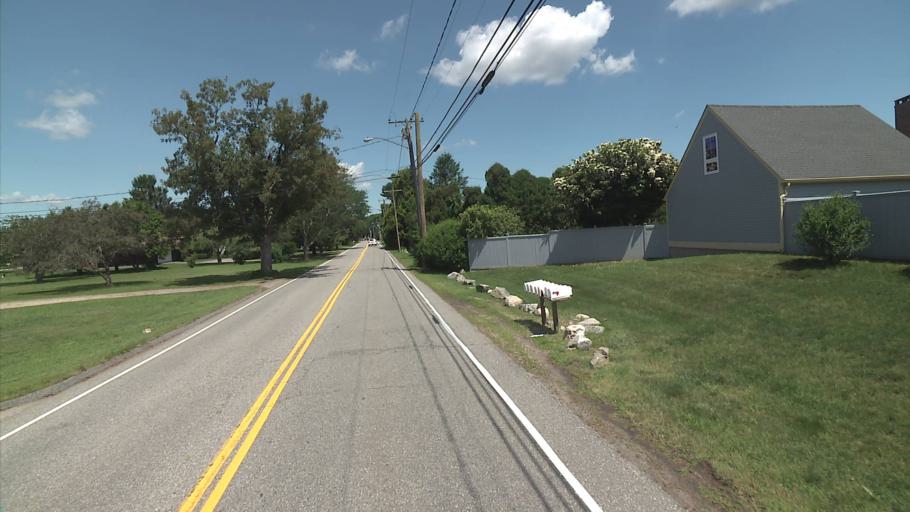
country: US
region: Connecticut
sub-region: New London County
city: Mystic
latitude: 41.3459
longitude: -71.9105
